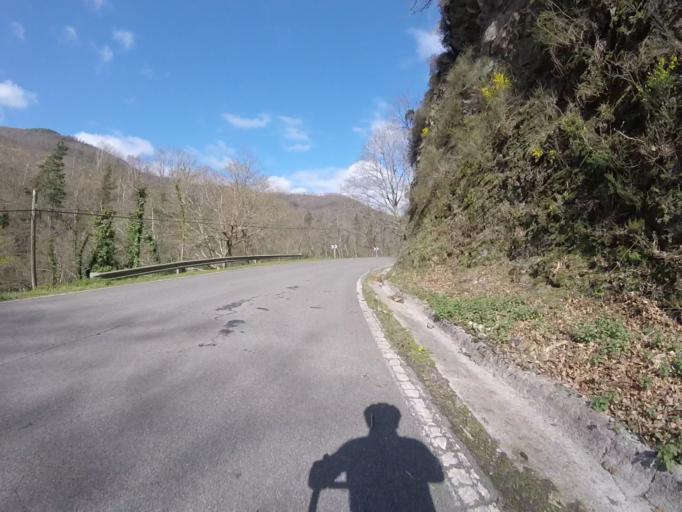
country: ES
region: Navarre
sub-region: Provincia de Navarra
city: Goizueta
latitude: 43.1443
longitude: -1.8502
